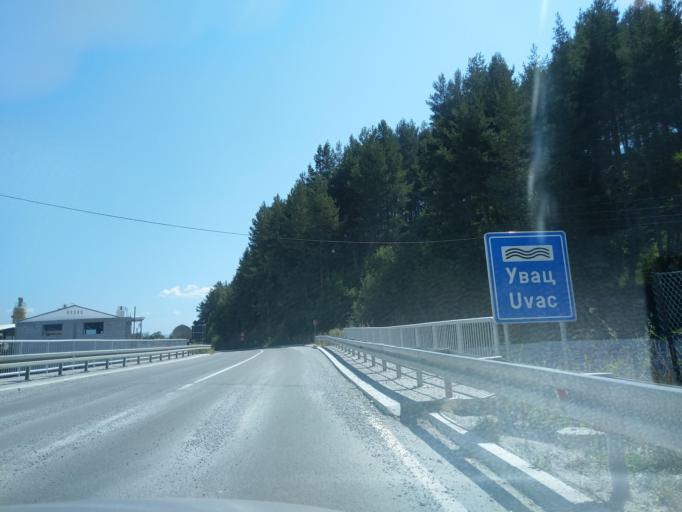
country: RS
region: Central Serbia
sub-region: Zlatiborski Okrug
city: Sjenica
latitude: 43.2812
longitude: 19.9648
